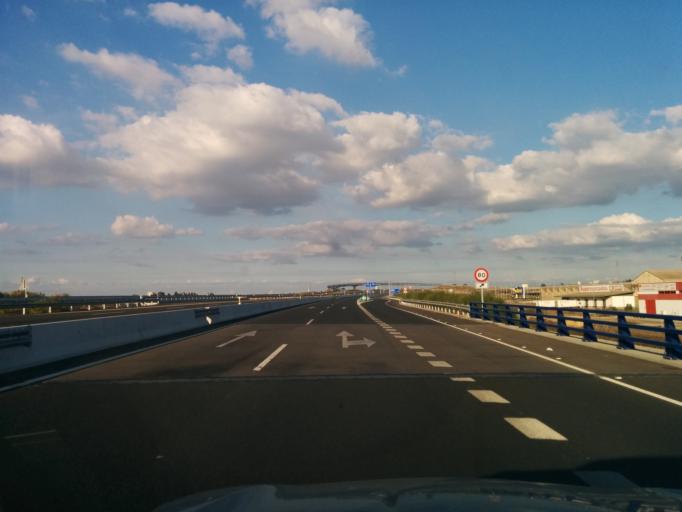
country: ES
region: Andalusia
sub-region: Provincia de Sevilla
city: Alcala de Guadaira
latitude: 37.3557
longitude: -5.8807
